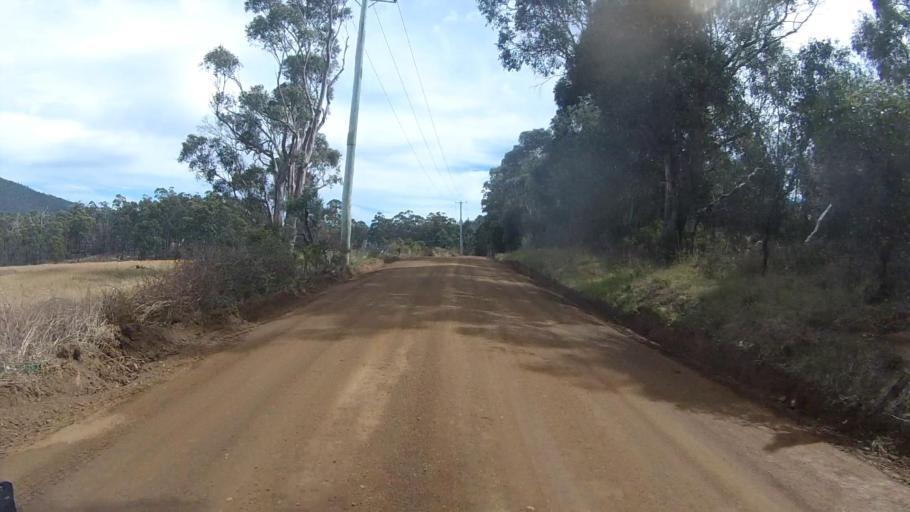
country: AU
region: Tasmania
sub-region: Sorell
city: Sorell
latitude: -42.7804
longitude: 147.8105
